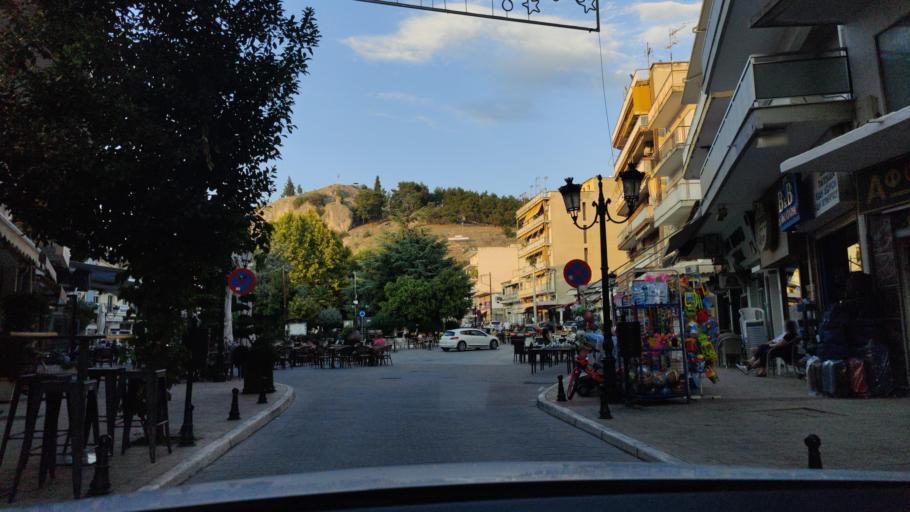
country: GR
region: Central Macedonia
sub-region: Nomos Serron
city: Sidirokastro
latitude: 41.2368
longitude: 23.3925
